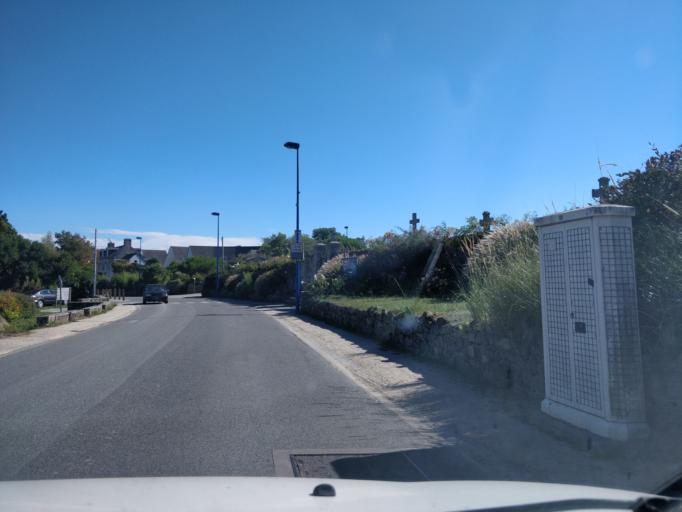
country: FR
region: Brittany
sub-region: Departement du Morbihan
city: Locmariaquer
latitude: 47.5716
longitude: -2.9479
